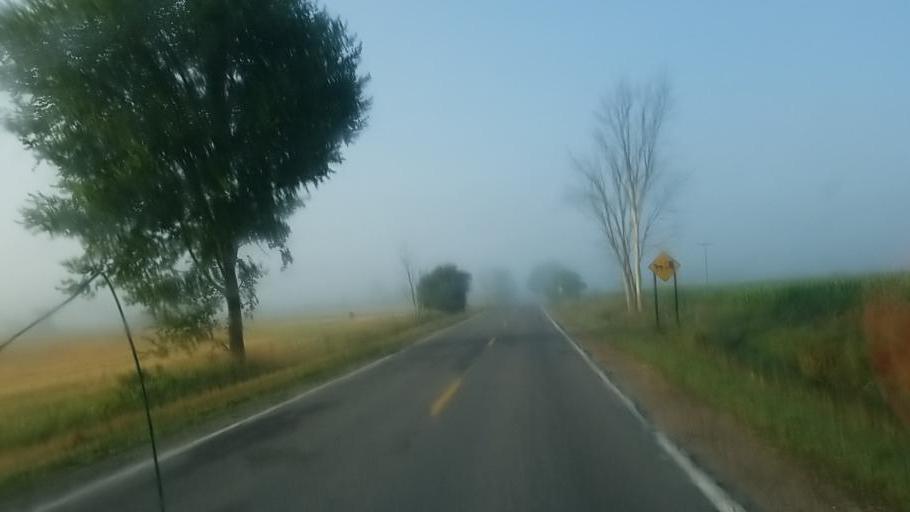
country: US
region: Michigan
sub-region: Muskegon County
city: Twin Lake
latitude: 43.4673
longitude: -86.0790
